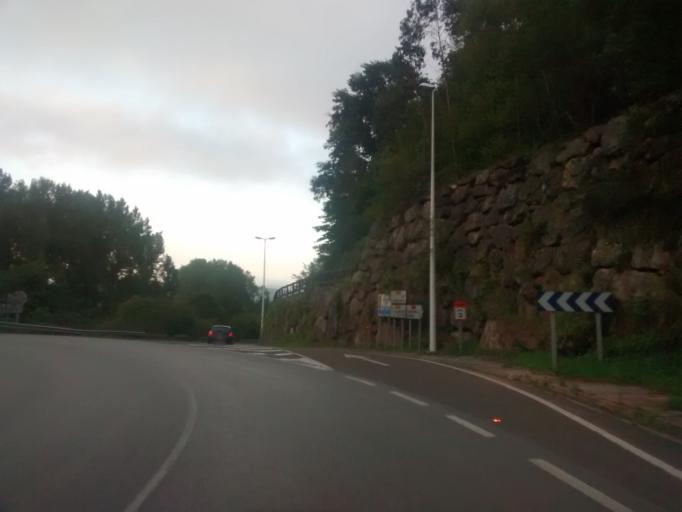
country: ES
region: Cantabria
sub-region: Provincia de Cantabria
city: Cabezon de la Sal
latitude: 43.2832
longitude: -4.2355
